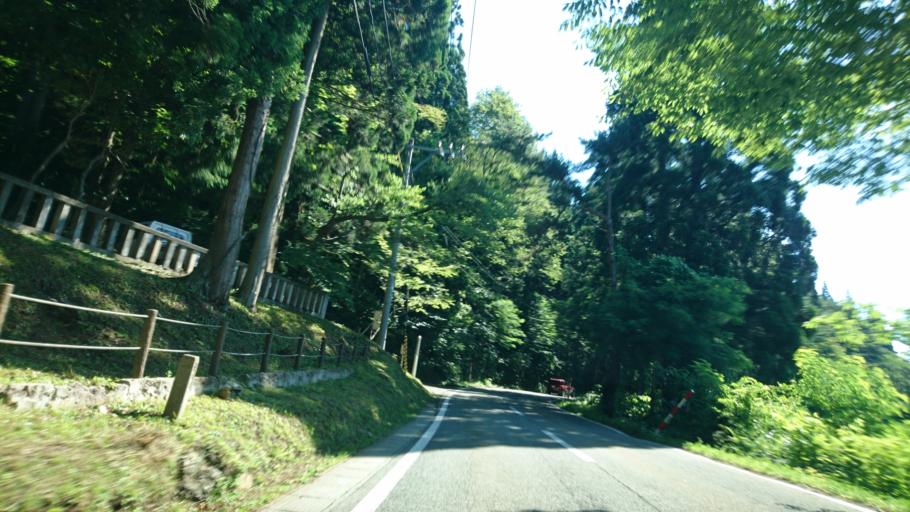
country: JP
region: Akita
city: Kakunodatemachi
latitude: 39.7513
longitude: 140.6507
